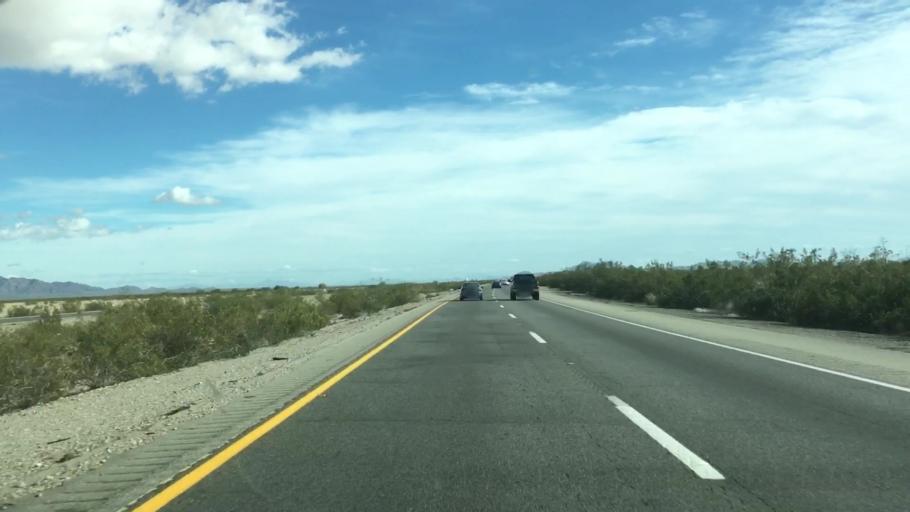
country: US
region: California
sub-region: Riverside County
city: Mesa Verde
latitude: 33.6205
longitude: -115.0347
